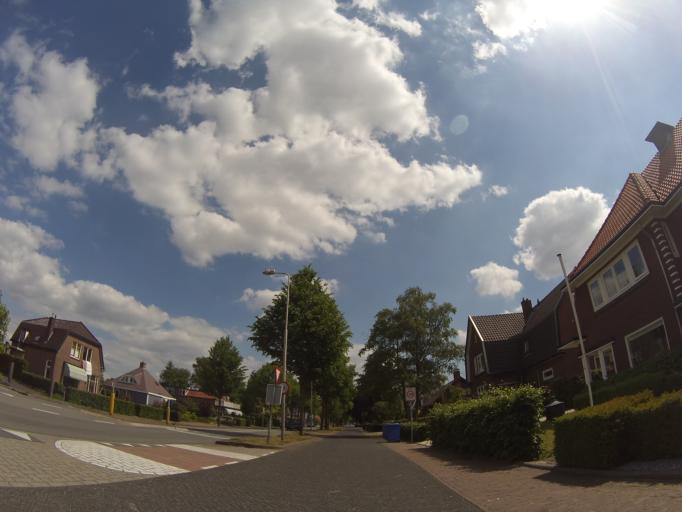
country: NL
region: Gelderland
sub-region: Gemeente Barneveld
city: Voorthuizen
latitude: 52.1823
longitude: 5.5952
